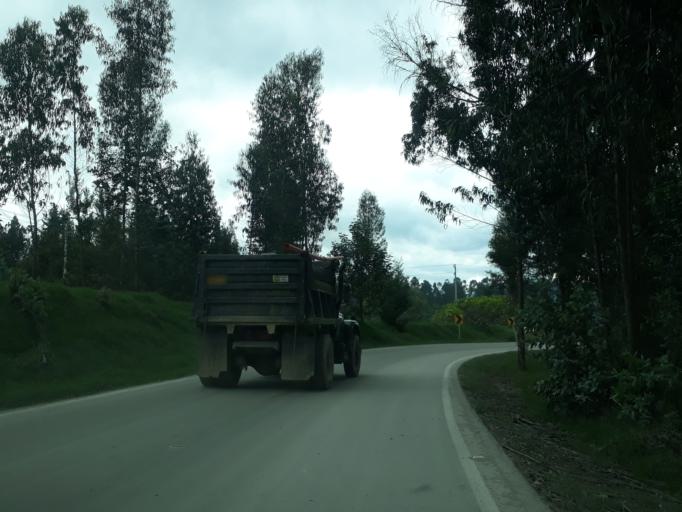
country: CO
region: Cundinamarca
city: Lenguazaque
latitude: 5.3280
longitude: -73.7529
